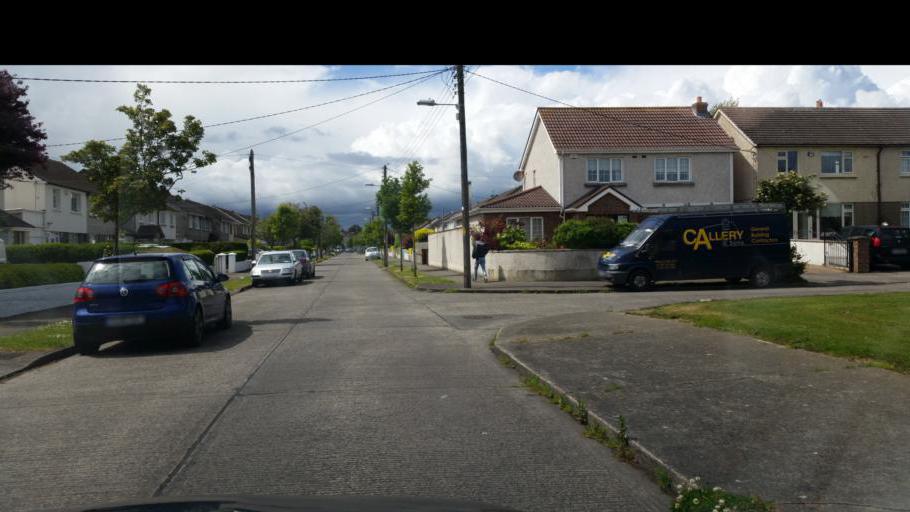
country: IE
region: Leinster
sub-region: Dublin City
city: Finglas
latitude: 53.3914
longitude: -6.2816
